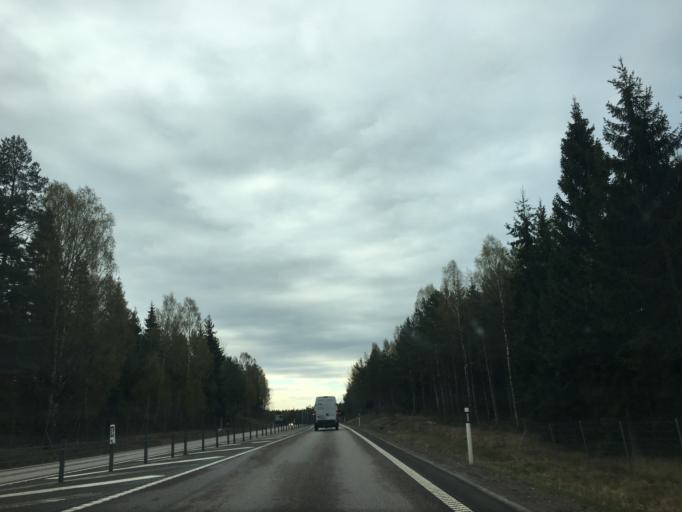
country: SE
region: Vaermland
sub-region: Kristinehamns Kommun
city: Kristinehamn
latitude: 59.3652
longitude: 14.0216
